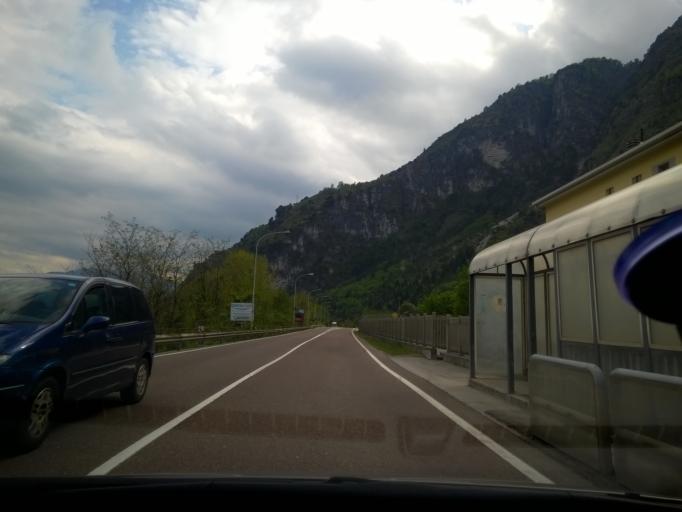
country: IT
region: Veneto
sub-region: Provincia di Belluno
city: Soverzene
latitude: 46.2263
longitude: 12.2878
